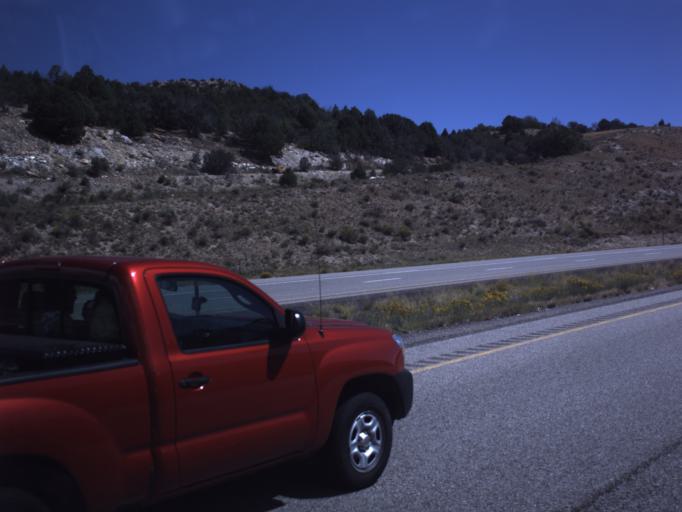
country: US
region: Utah
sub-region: Sevier County
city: Salina
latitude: 38.7828
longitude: -111.4897
